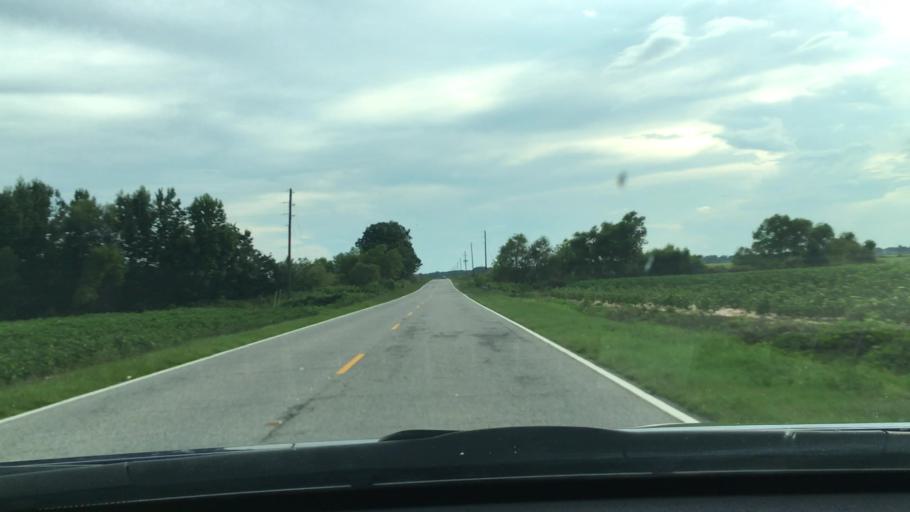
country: US
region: South Carolina
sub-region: Lee County
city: Bishopville
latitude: 34.0642
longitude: -80.2224
